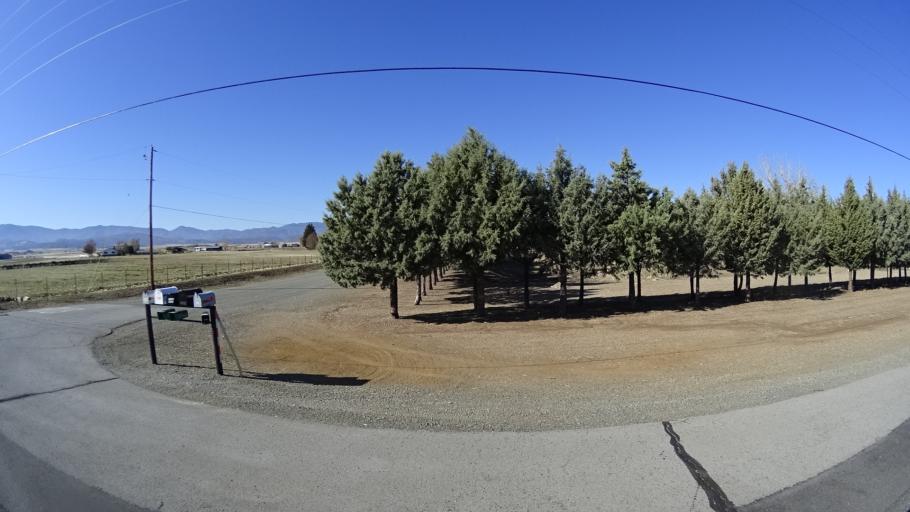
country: US
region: California
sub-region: Siskiyou County
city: Montague
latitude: 41.7519
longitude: -122.5248
